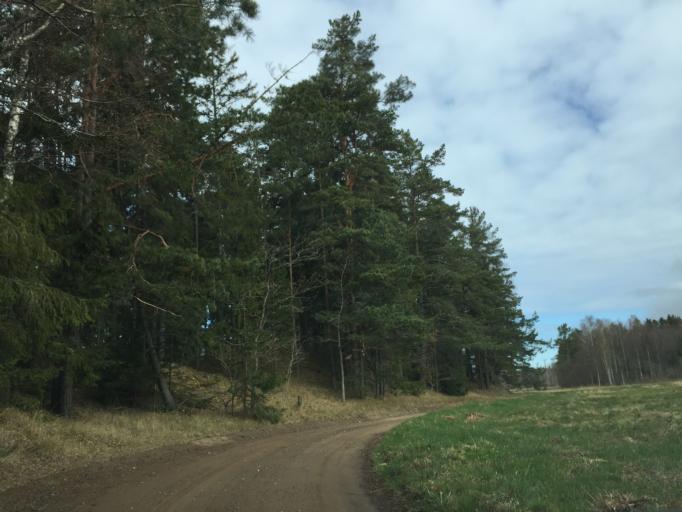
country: LV
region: Salacgrivas
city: Salacgriva
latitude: 57.5280
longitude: 24.3773
